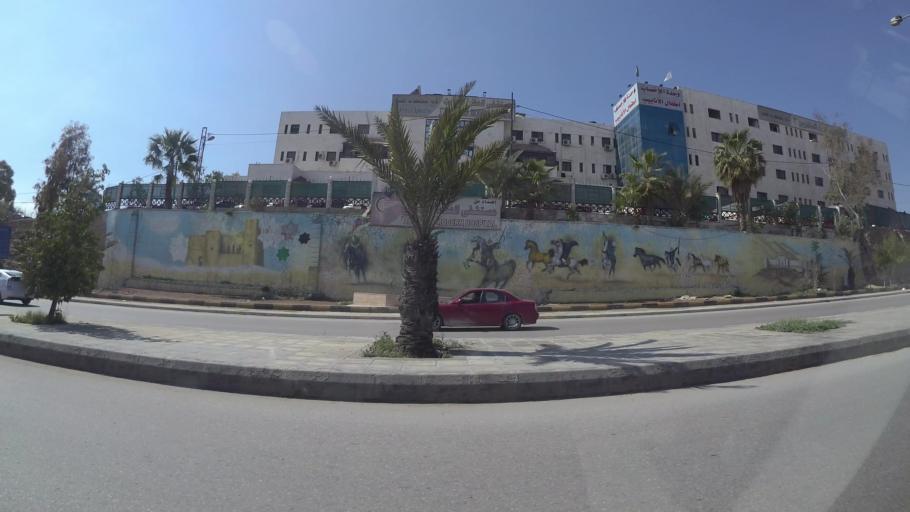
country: JO
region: Zarqa
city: Zarqa
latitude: 32.0533
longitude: 36.0943
